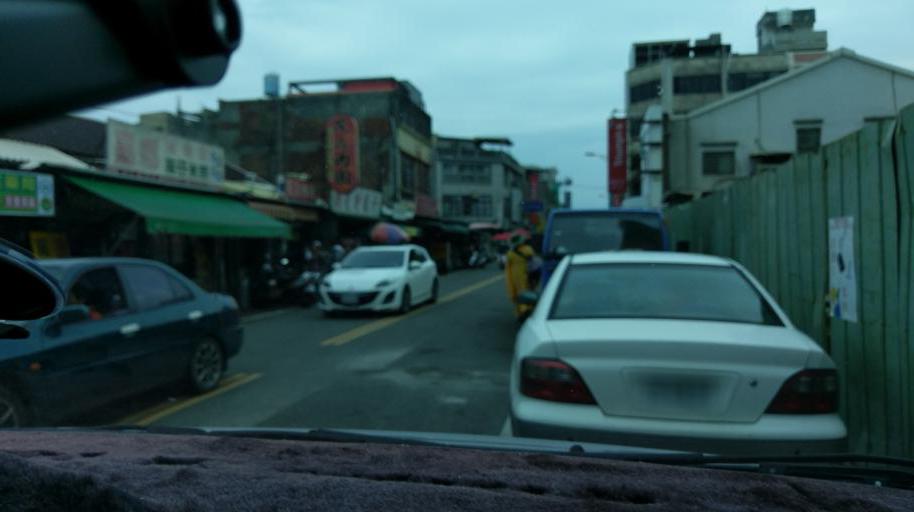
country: TW
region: Taiwan
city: Fengyuan
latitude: 24.4429
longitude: 120.6528
